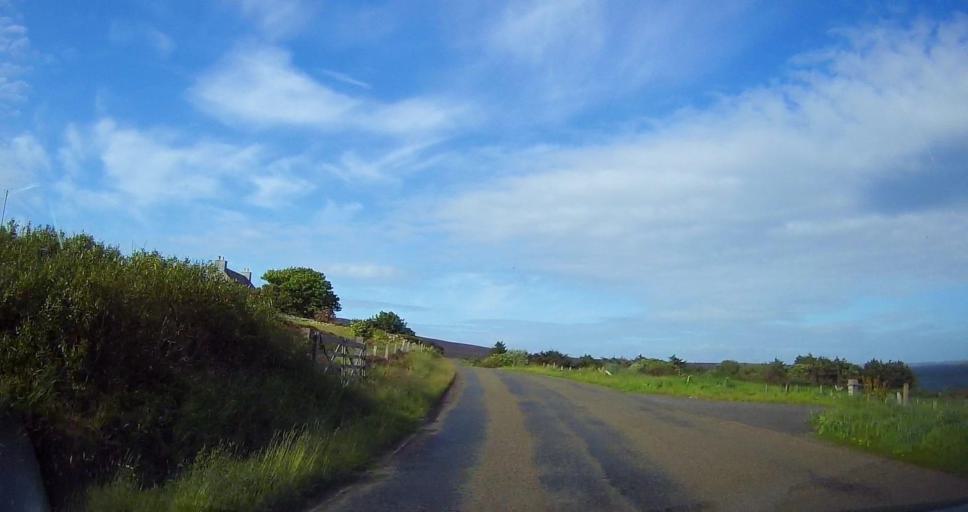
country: GB
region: Scotland
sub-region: Orkney Islands
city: Stromness
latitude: 58.7933
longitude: -3.2557
